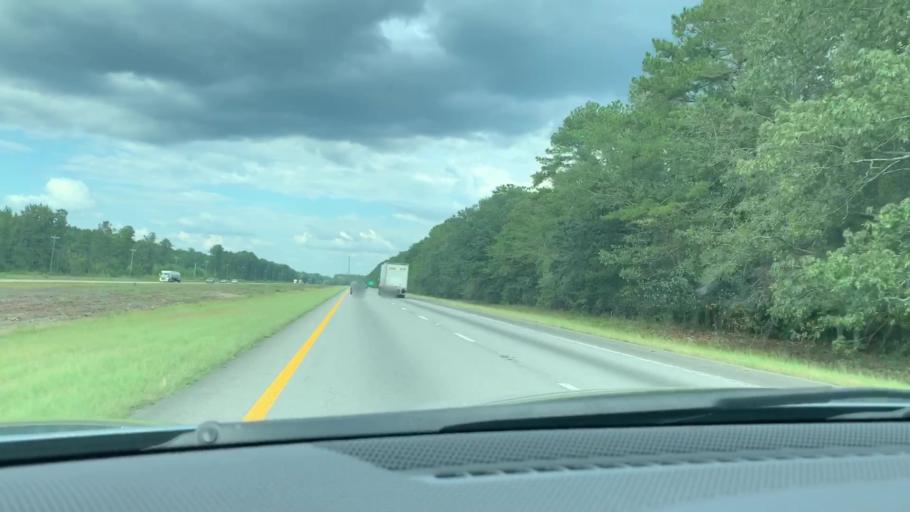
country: US
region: South Carolina
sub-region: Jasper County
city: Ridgeland
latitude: 32.5583
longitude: -80.9443
